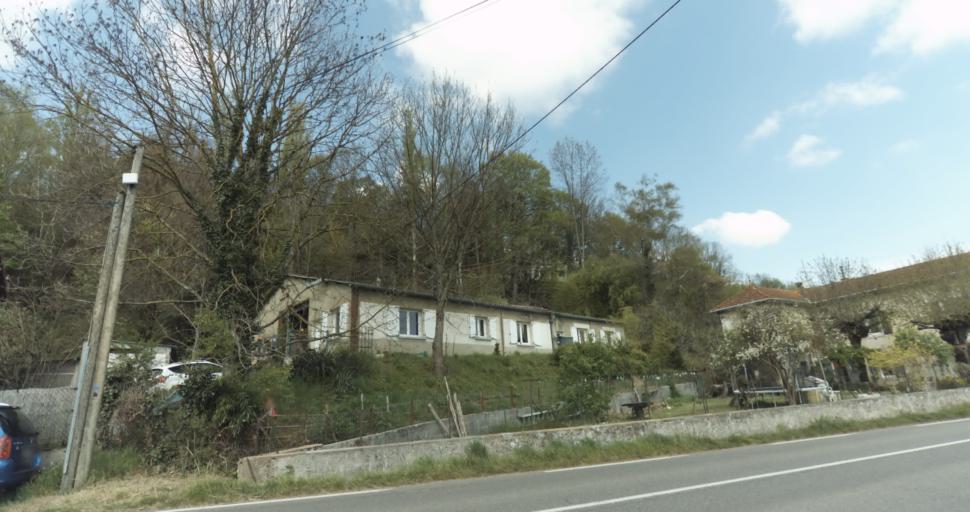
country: FR
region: Rhone-Alpes
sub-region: Departement de l'Isere
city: Saint-Verand
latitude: 45.1648
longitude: 5.3255
